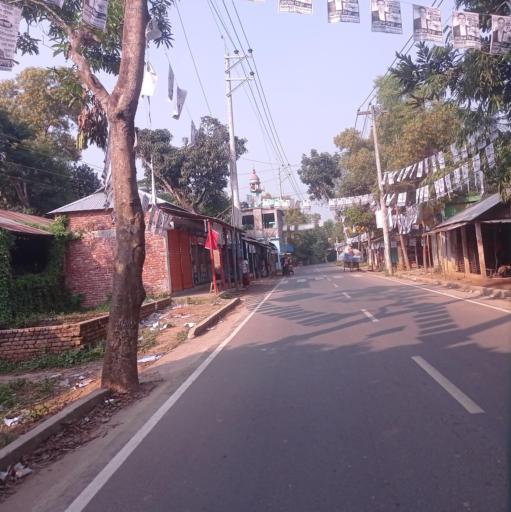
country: BD
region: Dhaka
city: Bhairab Bazar
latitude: 24.0455
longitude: 90.8347
